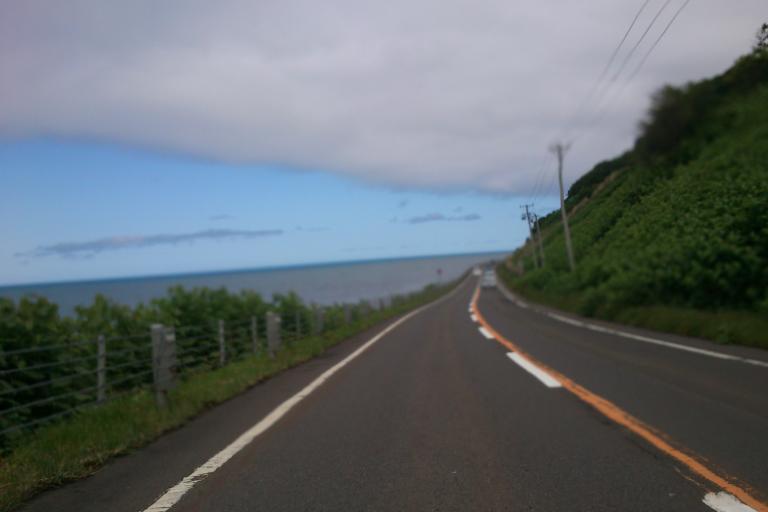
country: JP
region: Hokkaido
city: Ishikari
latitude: 43.4238
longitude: 141.4263
